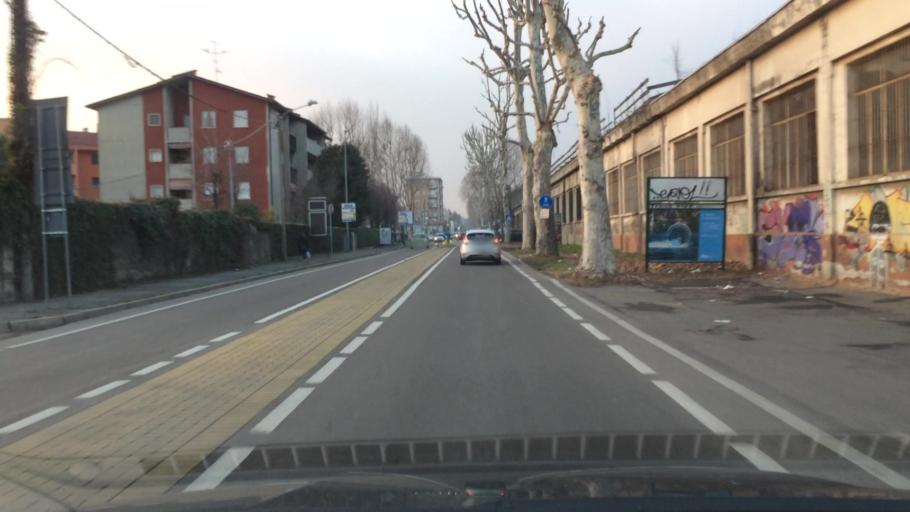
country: IT
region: Lombardy
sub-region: Provincia di Varese
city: Saronno
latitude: 45.6160
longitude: 9.0325
